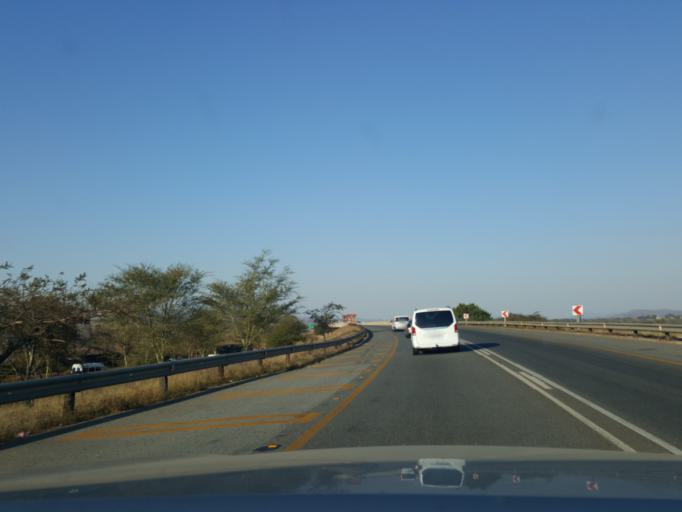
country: ZA
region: Mpumalanga
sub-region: Ehlanzeni District
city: Nelspruit
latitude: -25.4464
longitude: 30.9171
